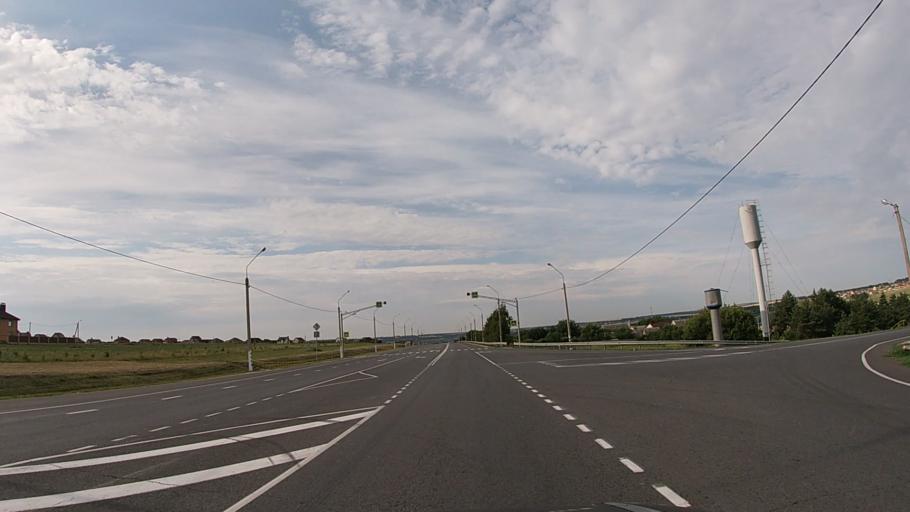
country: RU
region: Belgorod
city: Severnyy
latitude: 50.6529
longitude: 36.4673
